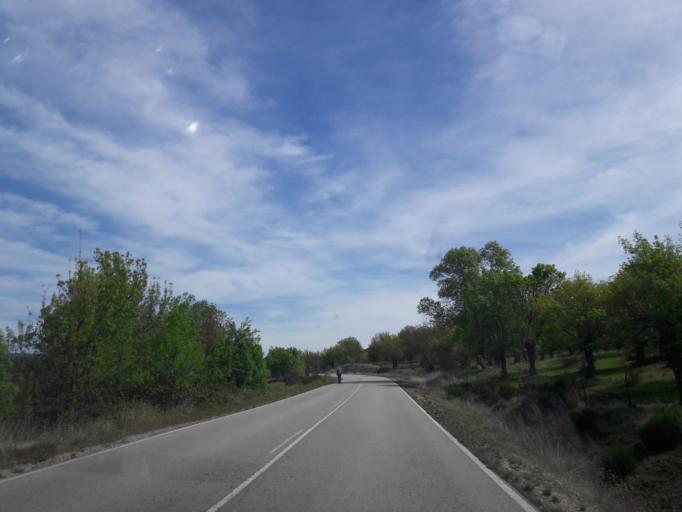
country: ES
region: Castille and Leon
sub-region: Provincia de Salamanca
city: Ledrada
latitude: 40.4551
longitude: -5.7327
